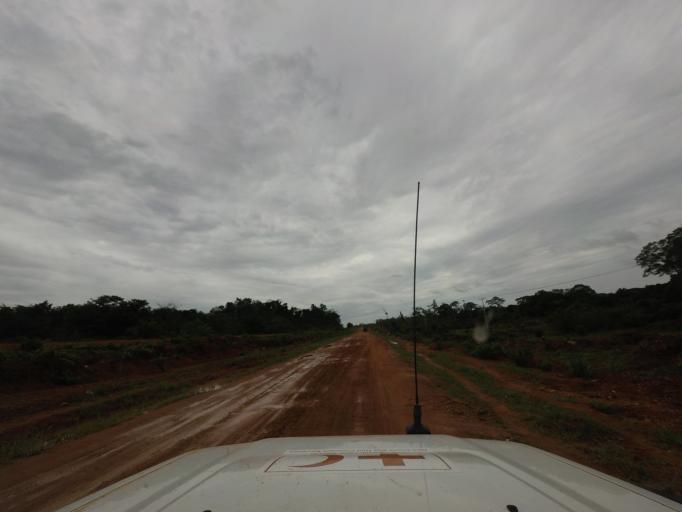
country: LR
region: Nimba
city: Sanniquellie
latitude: 7.2784
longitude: -8.8301
